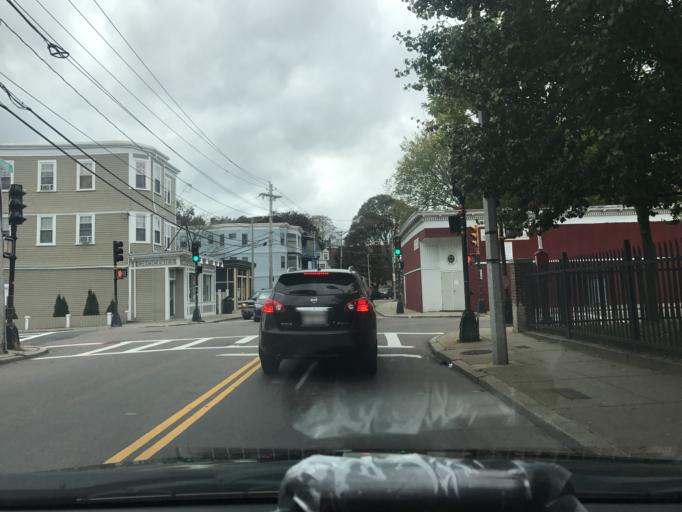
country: US
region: Massachusetts
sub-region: Suffolk County
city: Jamaica Plain
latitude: 42.2965
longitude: -71.0801
